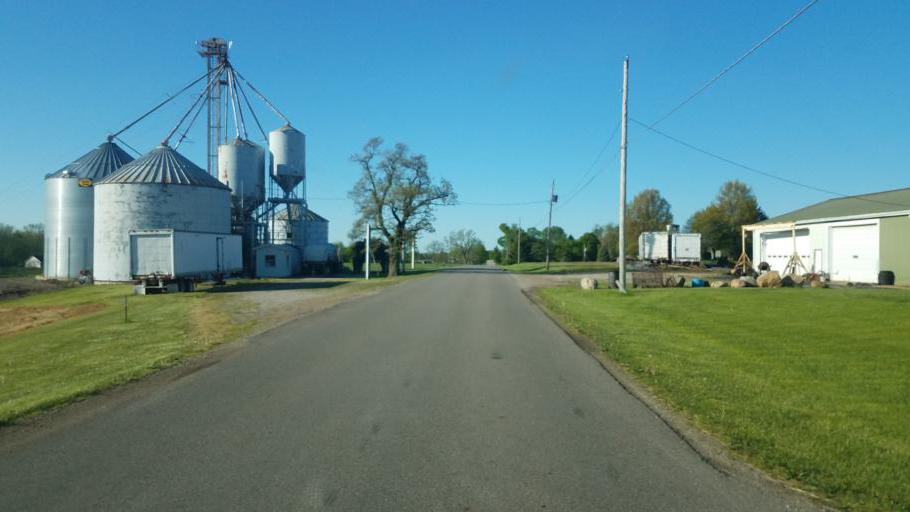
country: US
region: Ohio
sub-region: Morrow County
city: Cardington
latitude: 40.3900
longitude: -82.8129
